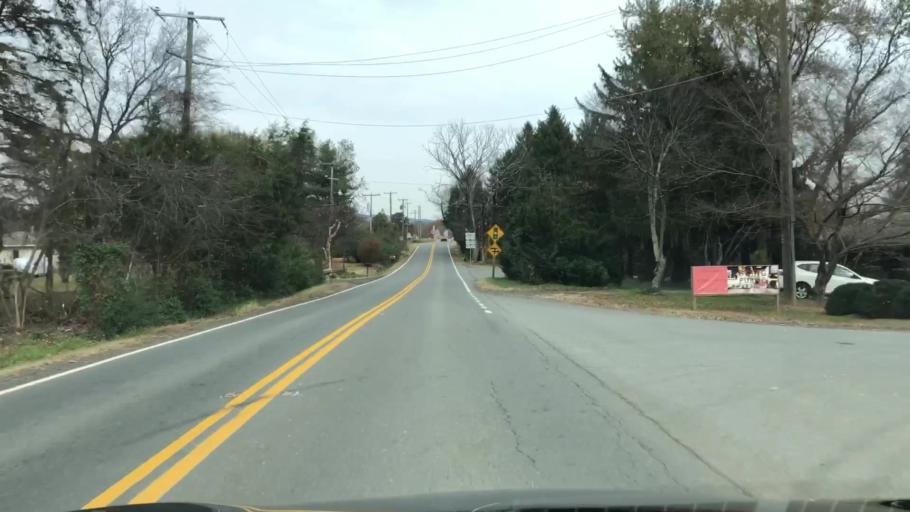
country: US
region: Virginia
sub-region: Fauquier County
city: New Baltimore
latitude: 38.7746
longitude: -77.6818
